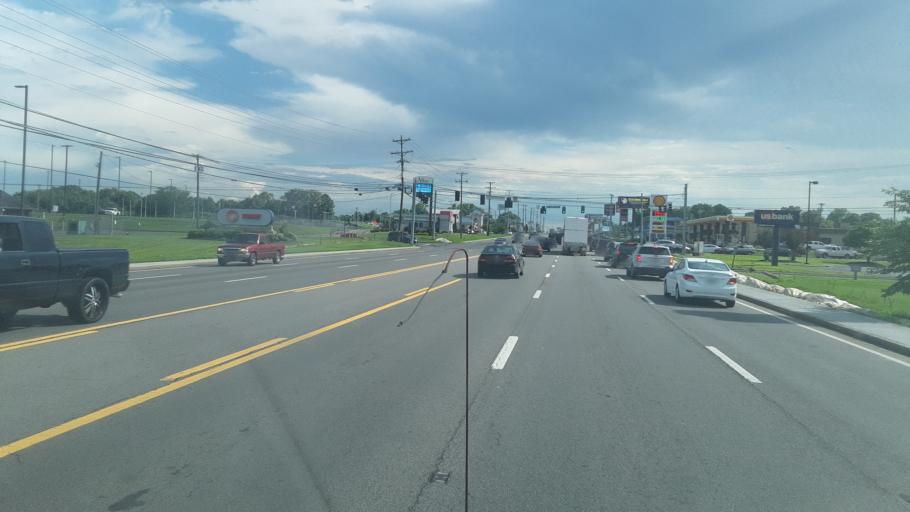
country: US
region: Tennessee
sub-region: Montgomery County
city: Clarksville
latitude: 36.5833
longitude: -87.2967
